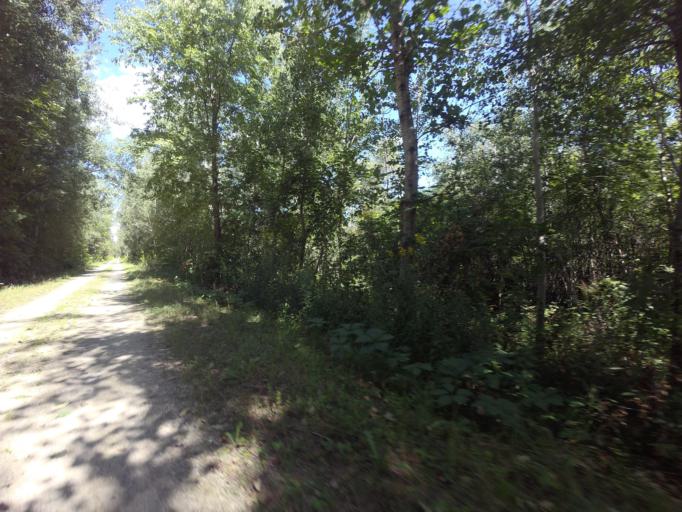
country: CA
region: Ontario
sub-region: Wellington County
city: Guelph
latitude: 43.7488
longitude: -80.3184
